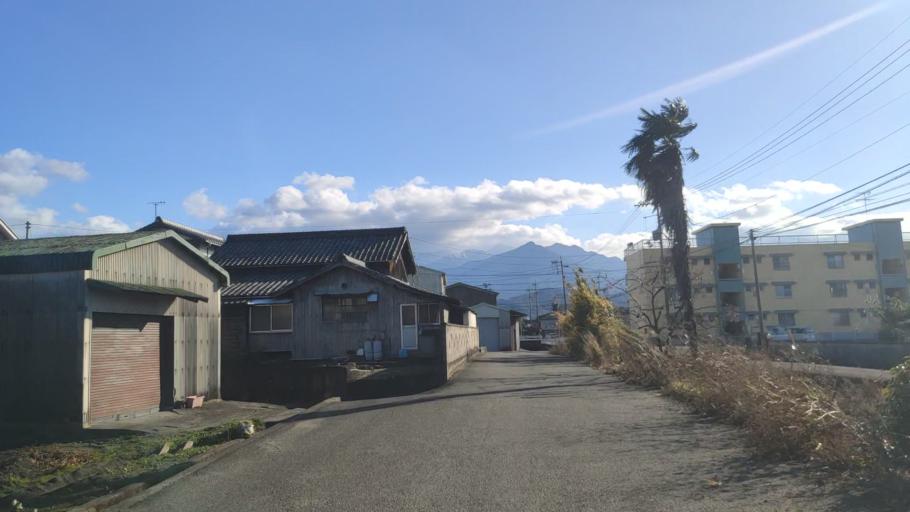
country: JP
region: Ehime
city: Saijo
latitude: 33.9209
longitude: 133.1621
